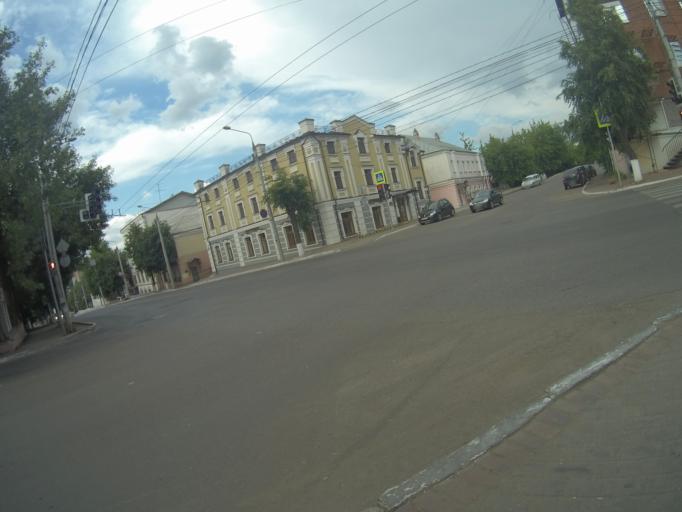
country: RU
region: Vladimir
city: Vladimir
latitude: 56.1313
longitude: 40.4027
